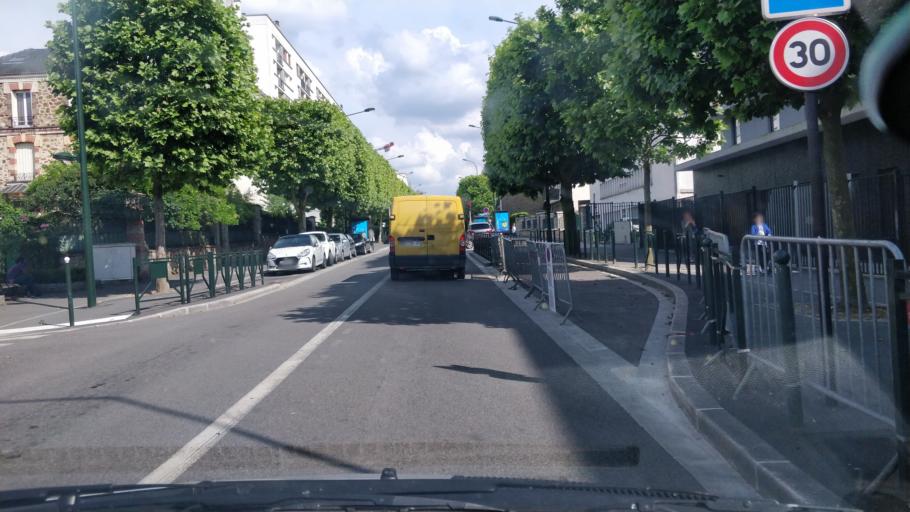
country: FR
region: Ile-de-France
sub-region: Departement de Seine-Saint-Denis
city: Le Raincy
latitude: 48.9011
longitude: 2.5129
